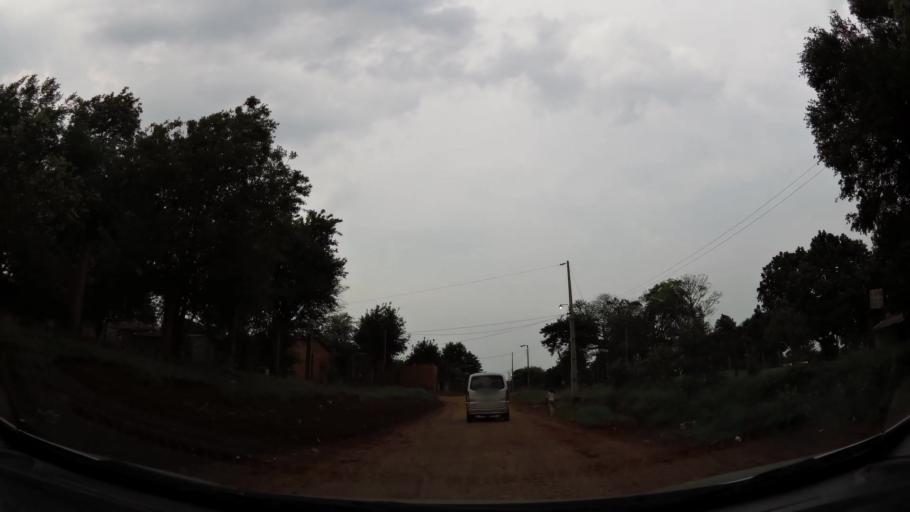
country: PY
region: Alto Parana
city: Presidente Franco
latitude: -25.5464
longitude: -54.6535
